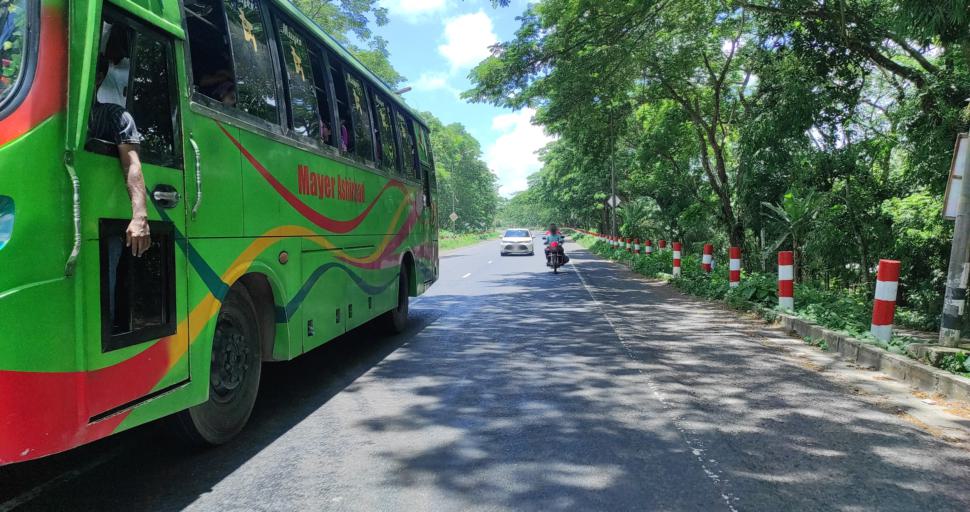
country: BD
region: Barisal
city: Gaurnadi
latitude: 22.8271
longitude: 90.2600
